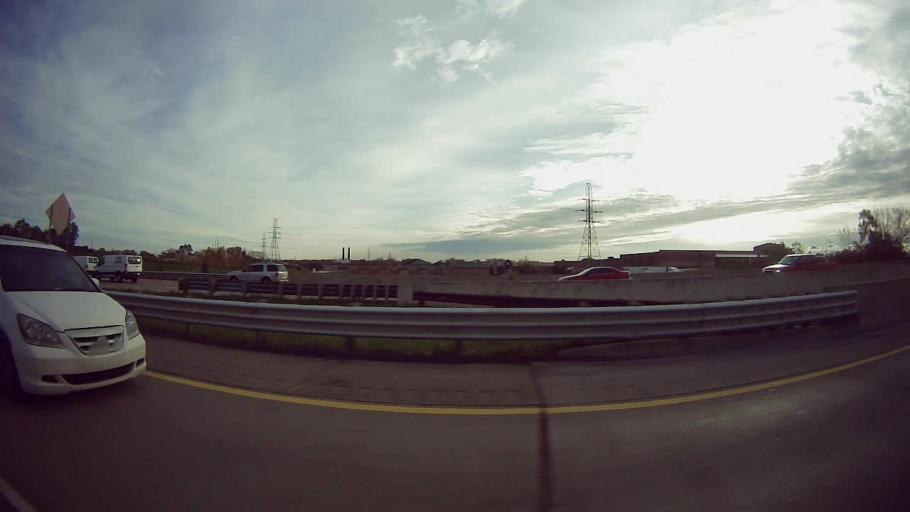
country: US
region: Michigan
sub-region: Oakland County
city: Madison Heights
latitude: 42.5070
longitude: -83.1151
